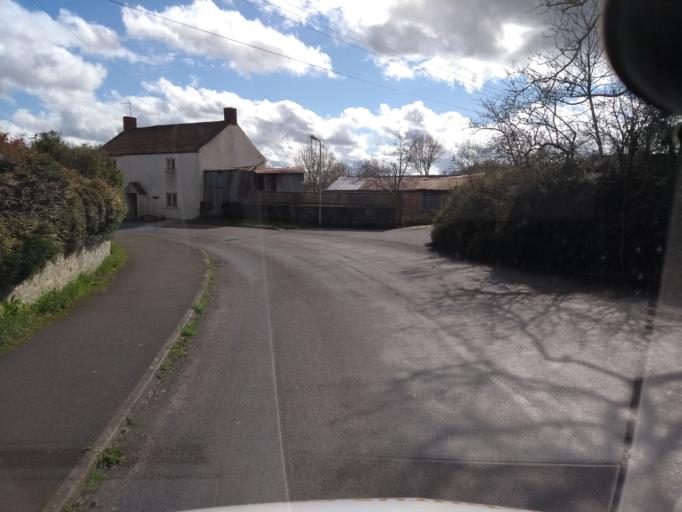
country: GB
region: England
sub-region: Somerset
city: Creech Saint Michael
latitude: 51.0269
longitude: -3.0659
